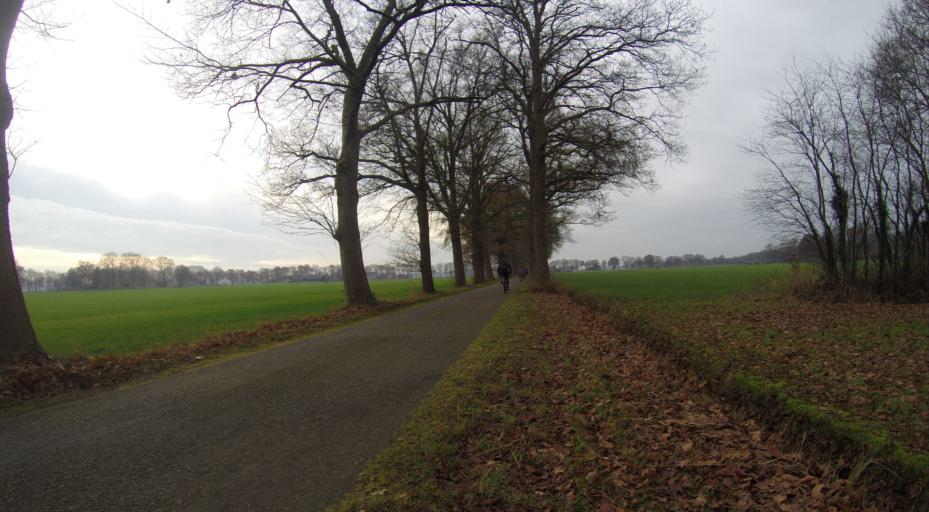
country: NL
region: Gelderland
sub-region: Gemeente Lochem
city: Lochem
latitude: 52.1392
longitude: 6.3966
